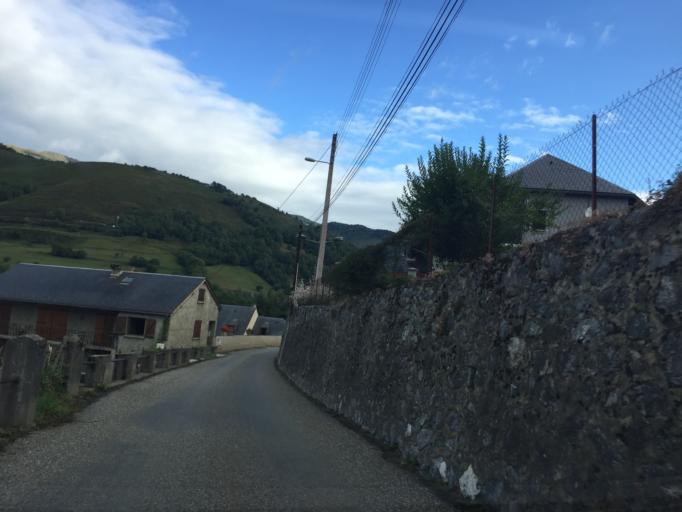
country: FR
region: Midi-Pyrenees
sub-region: Departement des Hautes-Pyrenees
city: Saint-Lary-Soulan
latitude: 42.9011
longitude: 0.3589
